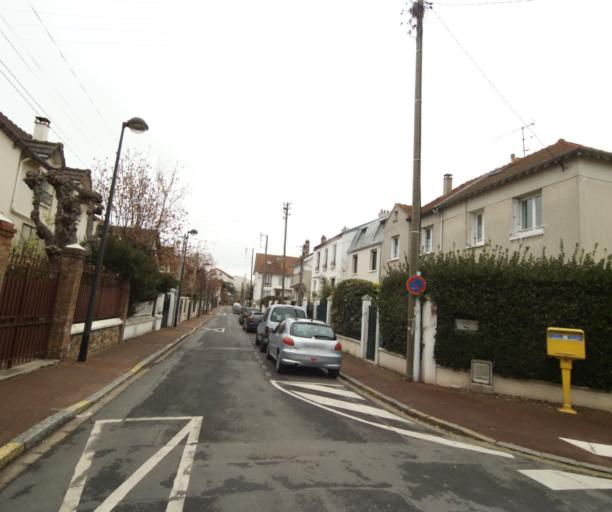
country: FR
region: Ile-de-France
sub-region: Departement des Yvelines
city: Chatou
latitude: 48.8856
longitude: 2.1676
